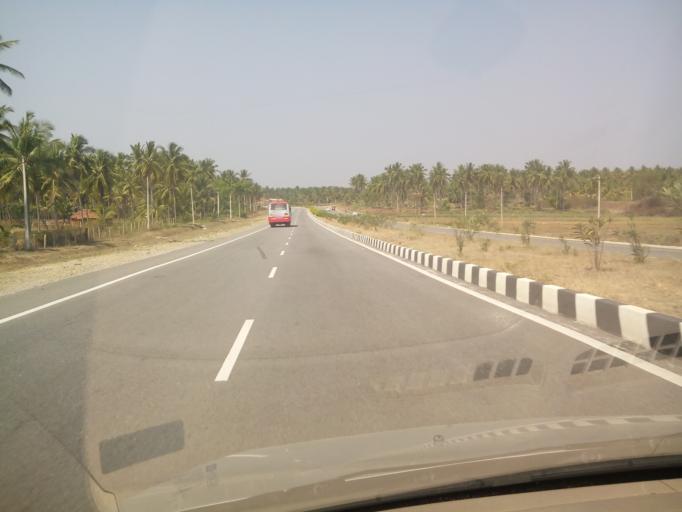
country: IN
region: Karnataka
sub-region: Hassan
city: Shravanabelagola
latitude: 12.9163
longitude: 76.4608
